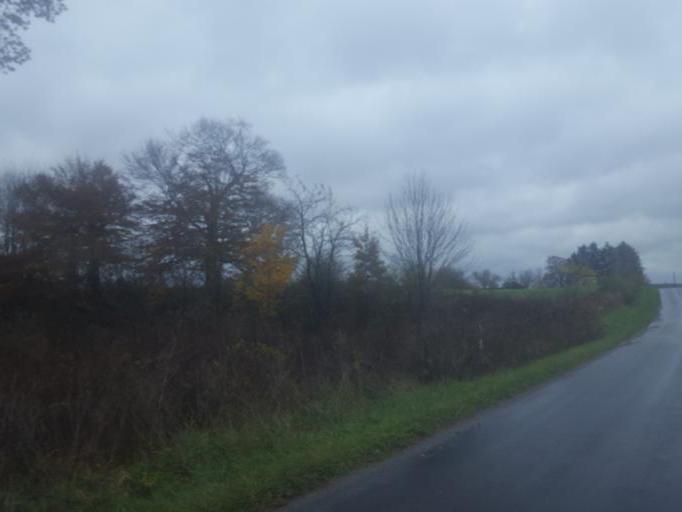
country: US
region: Ohio
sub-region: Knox County
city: Fredericktown
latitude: 40.5414
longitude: -82.5883
